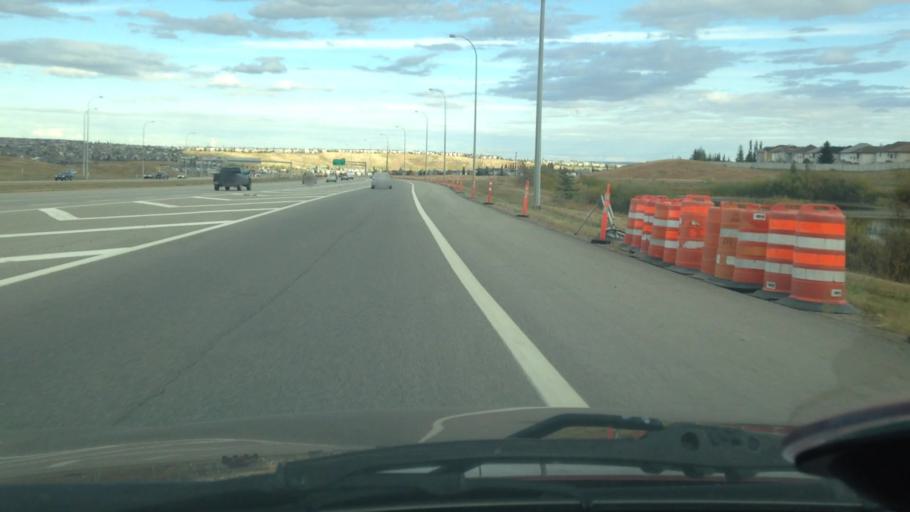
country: CA
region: Alberta
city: Calgary
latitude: 51.1519
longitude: -114.1359
